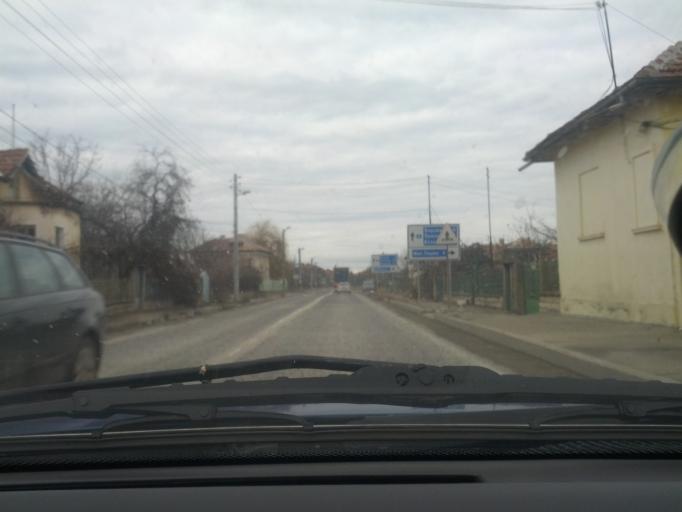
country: BG
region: Vratsa
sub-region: Obshtina Borovan
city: Borovan
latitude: 43.3445
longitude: 23.6923
